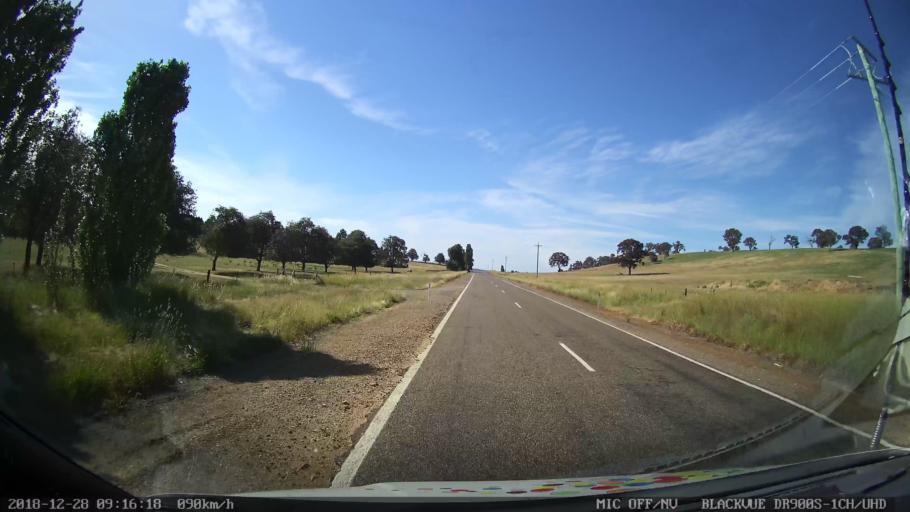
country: AU
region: New South Wales
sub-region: Upper Lachlan Shire
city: Crookwell
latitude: -34.3067
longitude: 149.3549
